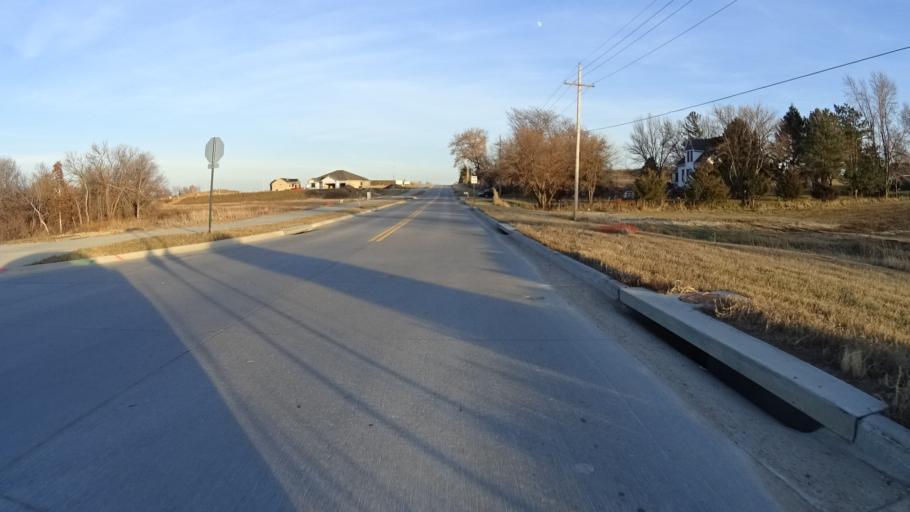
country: US
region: Nebraska
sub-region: Sarpy County
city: Papillion
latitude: 41.1326
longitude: -96.0821
